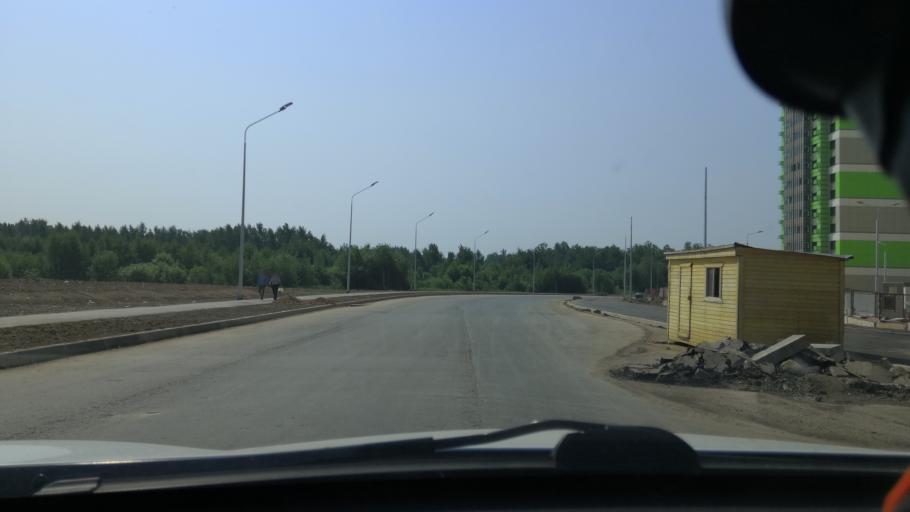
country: RU
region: Moscow
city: Severnyy
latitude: 55.9402
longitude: 37.5312
